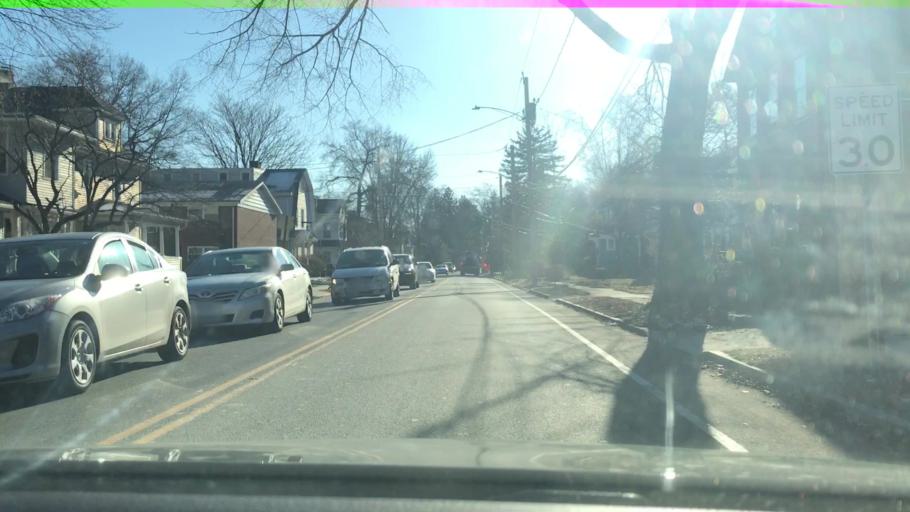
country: US
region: Connecticut
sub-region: New Haven County
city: New Haven
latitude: 41.3269
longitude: -72.9683
